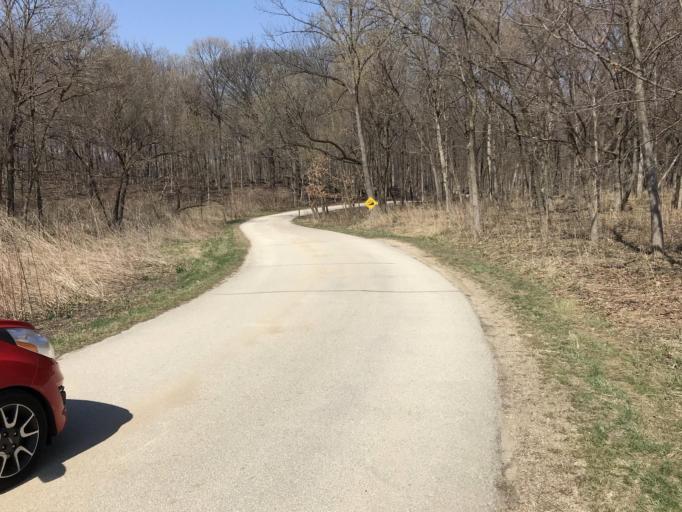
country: US
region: Illinois
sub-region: DuPage County
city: Downers Grove
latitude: 41.8134
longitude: -88.0378
